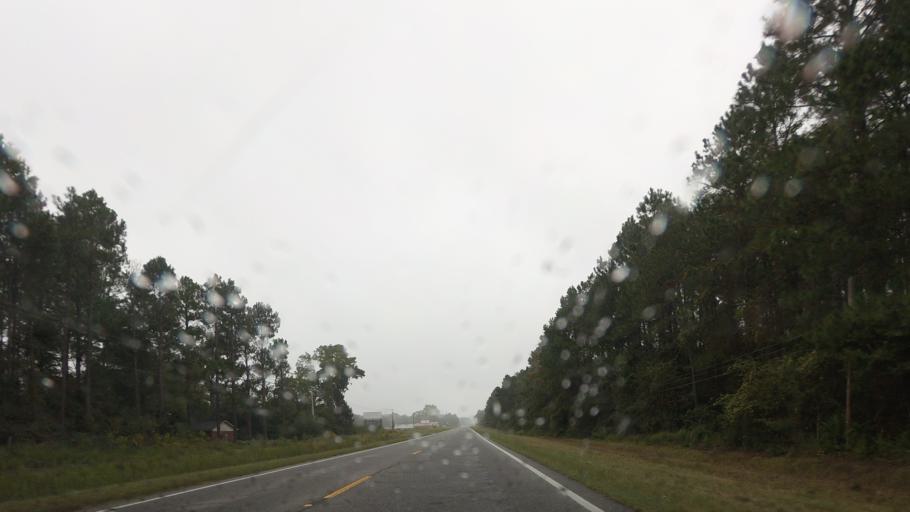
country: US
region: Georgia
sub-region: Ben Hill County
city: Fitzgerald
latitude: 31.7391
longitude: -83.2462
